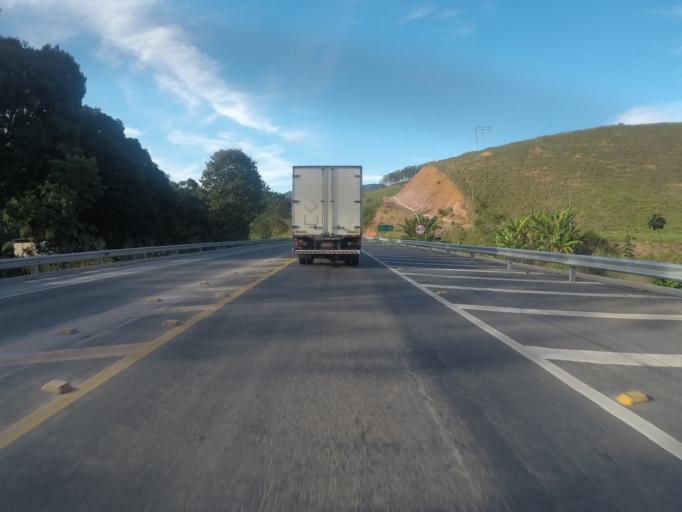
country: BR
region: Espirito Santo
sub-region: Ibiracu
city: Ibiracu
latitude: -19.8391
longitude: -40.3832
